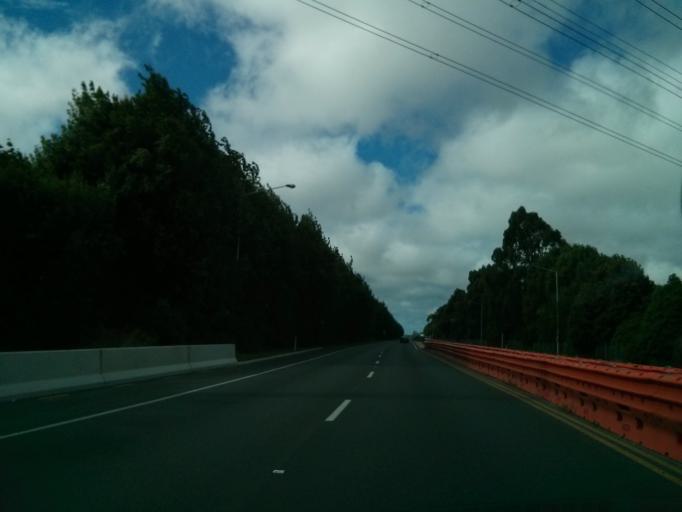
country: NZ
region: Canterbury
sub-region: Selwyn District
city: Prebbleton
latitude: -43.5119
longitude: 172.5389
